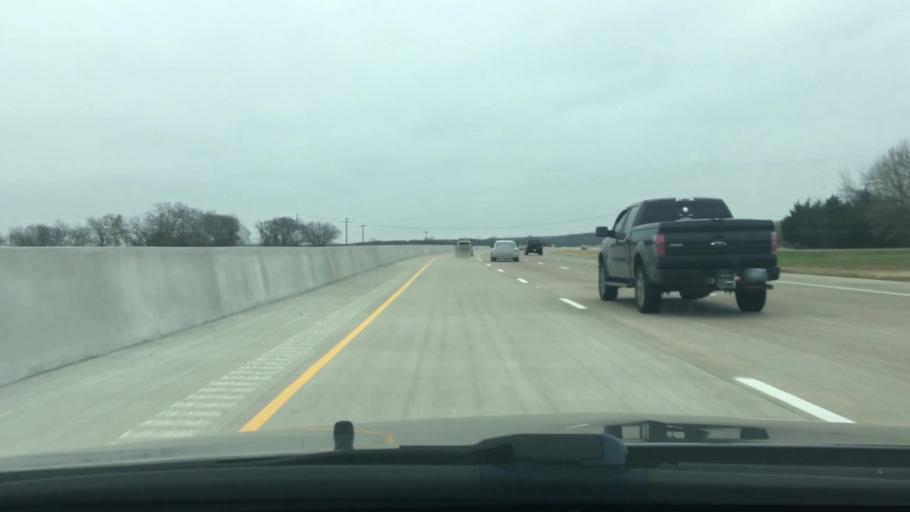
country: US
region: Texas
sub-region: Freestone County
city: Wortham
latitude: 31.9273
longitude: -96.4177
